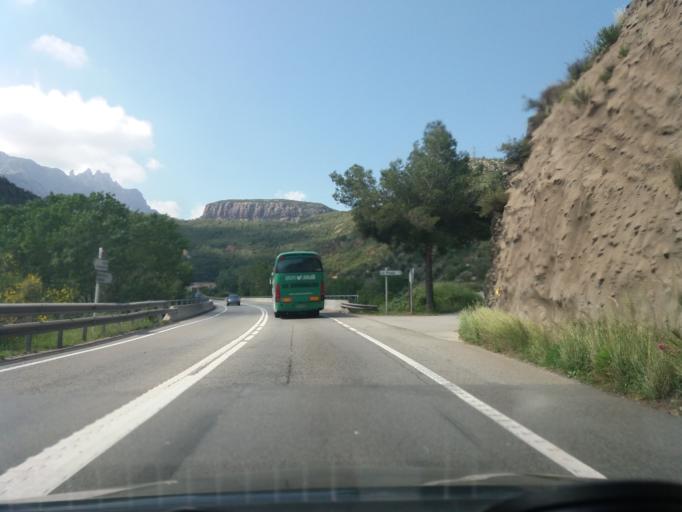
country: ES
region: Catalonia
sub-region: Provincia de Barcelona
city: Olesa de Montserrat
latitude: 41.5665
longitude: 1.8805
